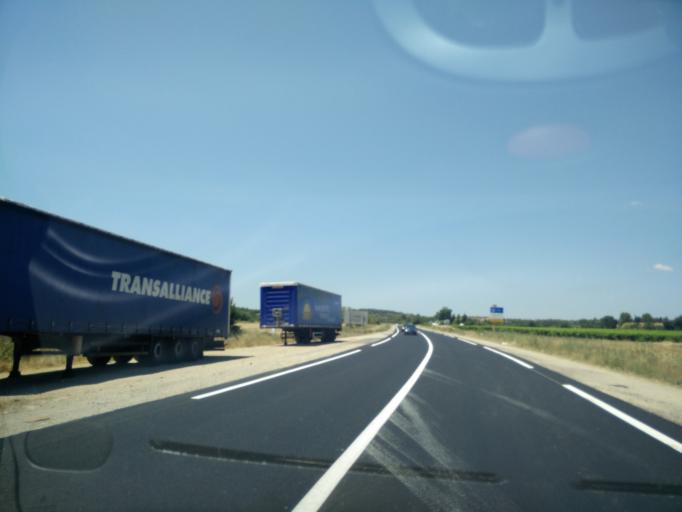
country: FR
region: Languedoc-Roussillon
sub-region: Departement de l'Herault
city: Lunel
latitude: 43.6925
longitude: 4.1431
